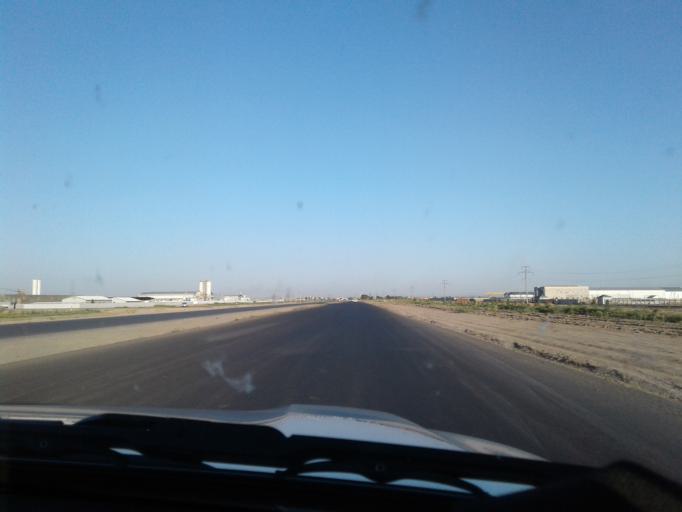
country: TM
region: Mary
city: Mary
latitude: 37.5774
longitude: 61.7975
